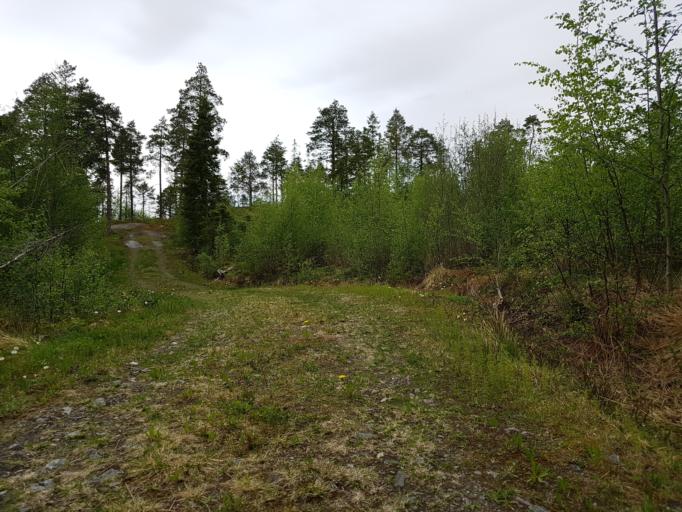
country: NO
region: Nord-Trondelag
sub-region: Levanger
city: Skogn
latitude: 63.6321
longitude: 11.2542
